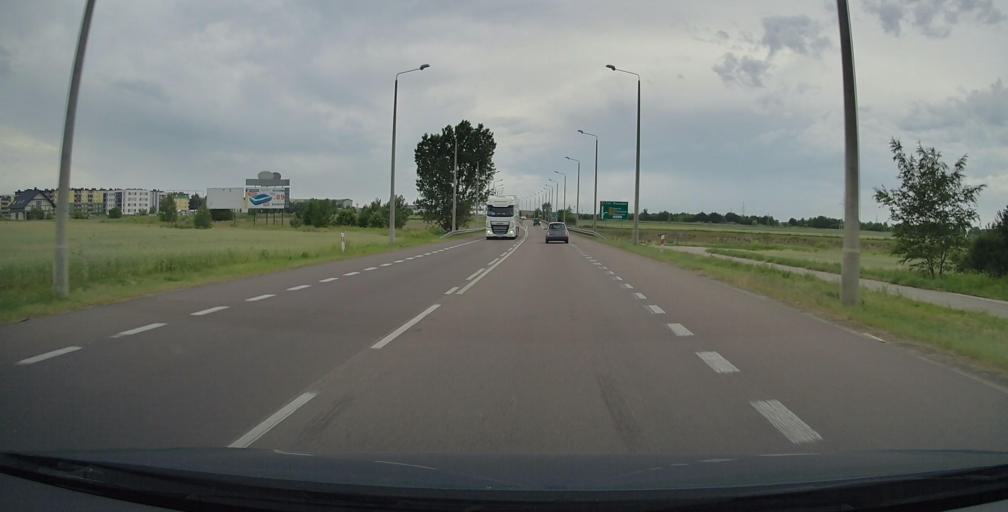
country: PL
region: Lublin Voivodeship
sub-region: Biala Podlaska
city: Biala Podlaska
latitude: 52.0524
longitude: 23.1291
